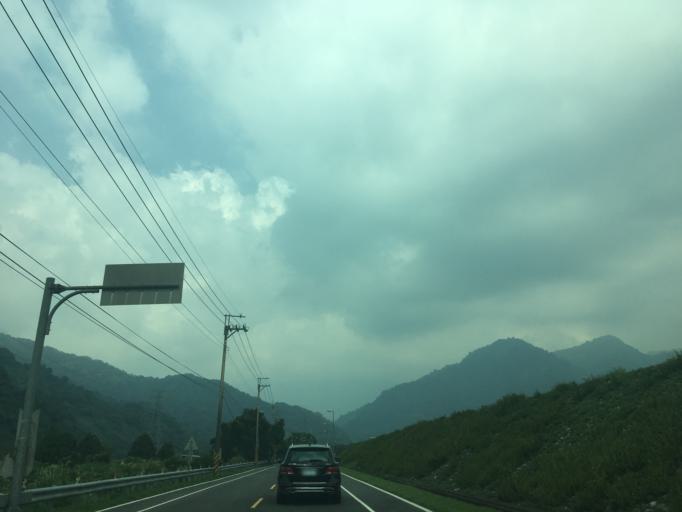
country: TW
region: Taiwan
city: Fengyuan
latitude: 24.2962
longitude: 120.8887
